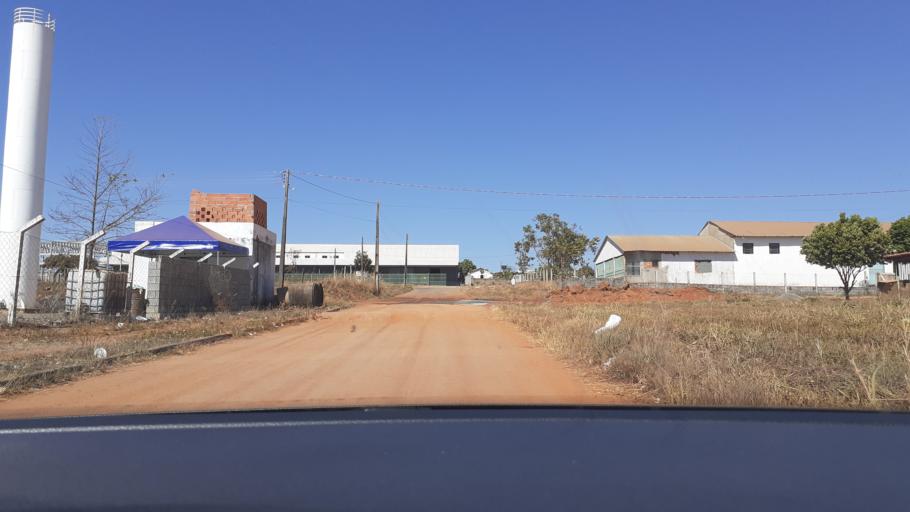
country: BR
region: Goias
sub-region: Aparecida De Goiania
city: Aparecida de Goiania
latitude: -16.8786
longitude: -49.2548
